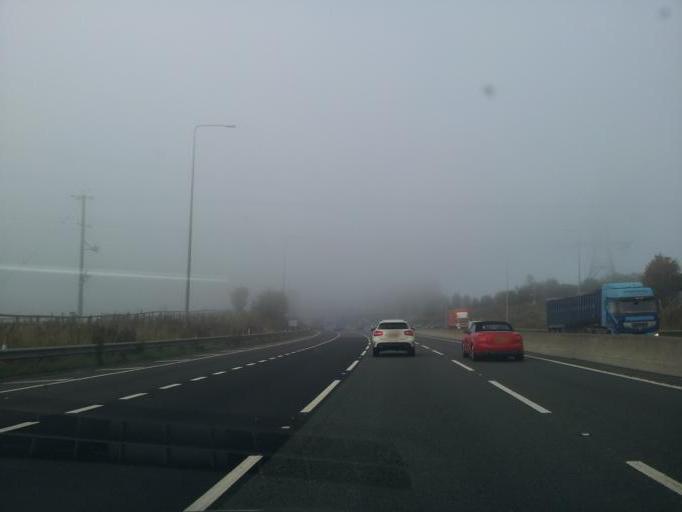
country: GB
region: England
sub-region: Kirklees
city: Cleckheaton
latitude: 53.7457
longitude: -1.7112
